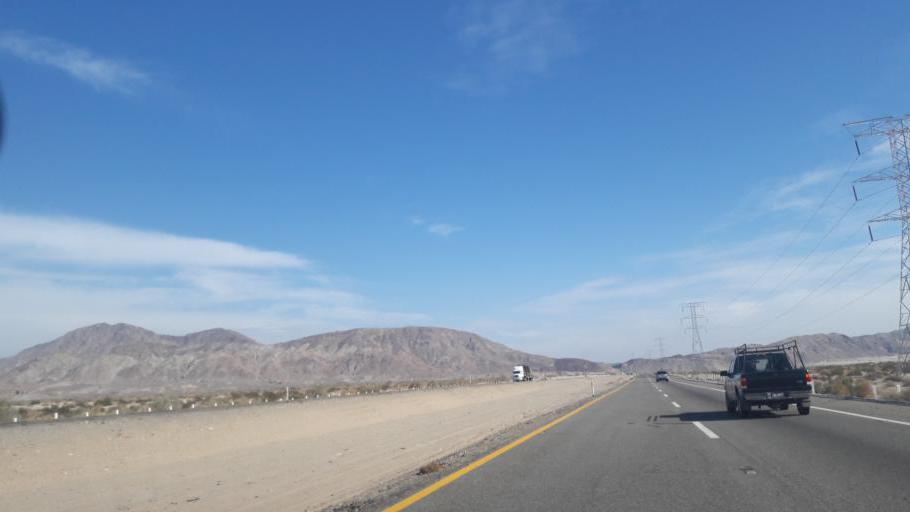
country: MX
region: Baja California
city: Progreso
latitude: 32.5742
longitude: -115.7664
